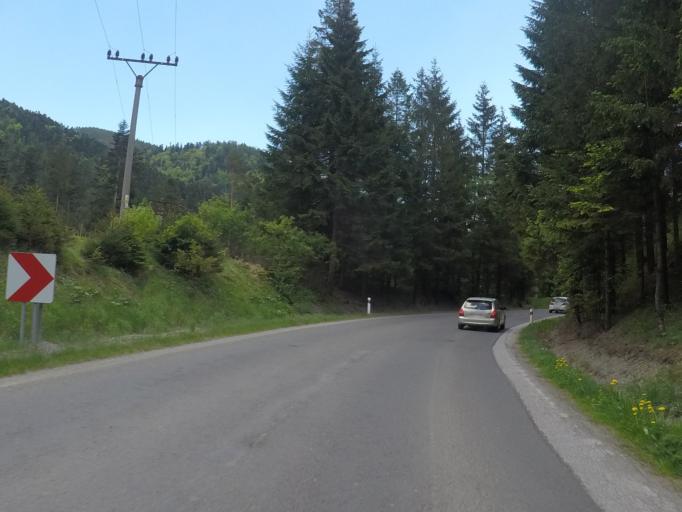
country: SK
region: Presovsky
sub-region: Okres Poprad
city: Zdiar
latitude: 49.2489
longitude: 20.3104
